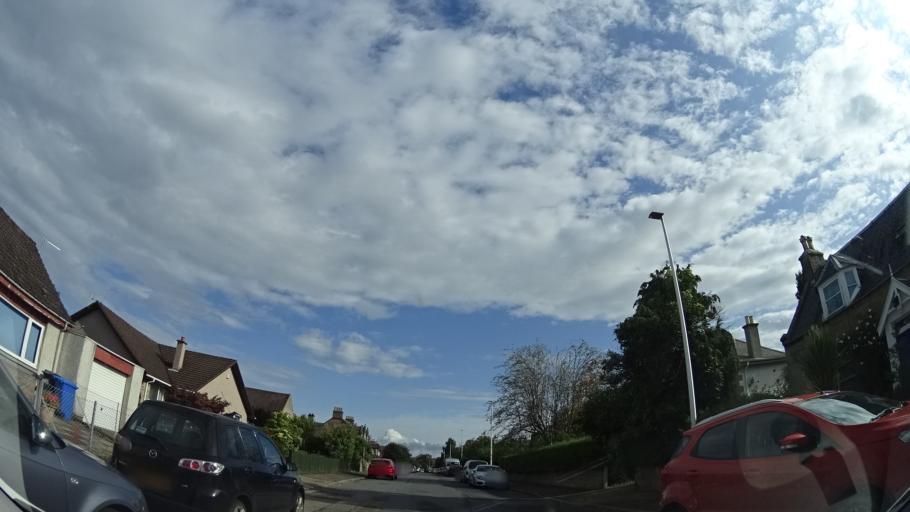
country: GB
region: Scotland
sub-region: Highland
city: Inverness
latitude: 57.4699
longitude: -4.2346
